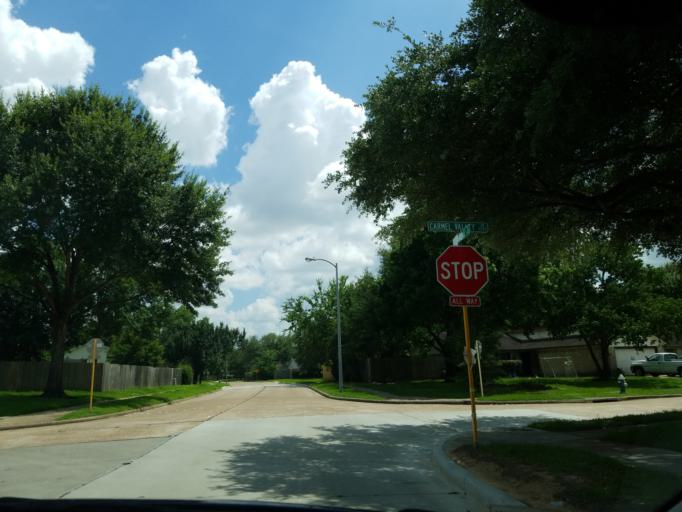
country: US
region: Texas
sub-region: Harris County
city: Cypress
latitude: 29.8760
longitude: -95.7325
